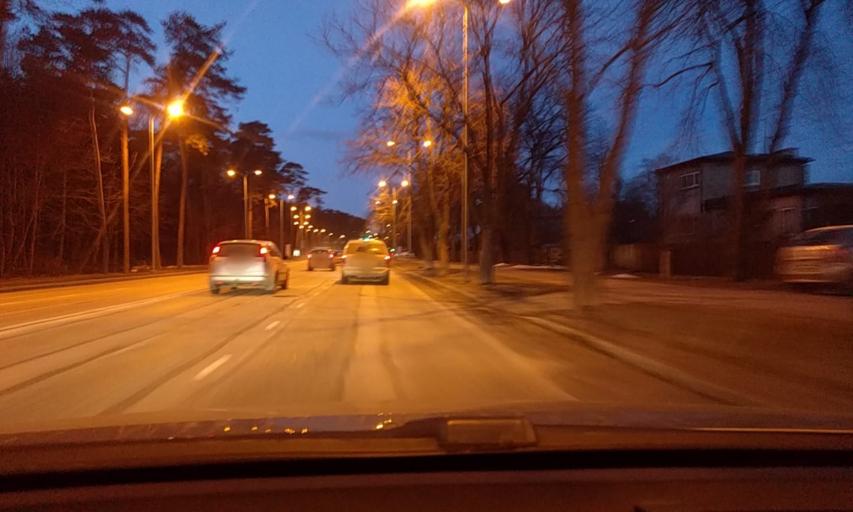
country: EE
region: Harju
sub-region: Viimsi vald
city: Viimsi
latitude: 59.4723
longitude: 24.8362
